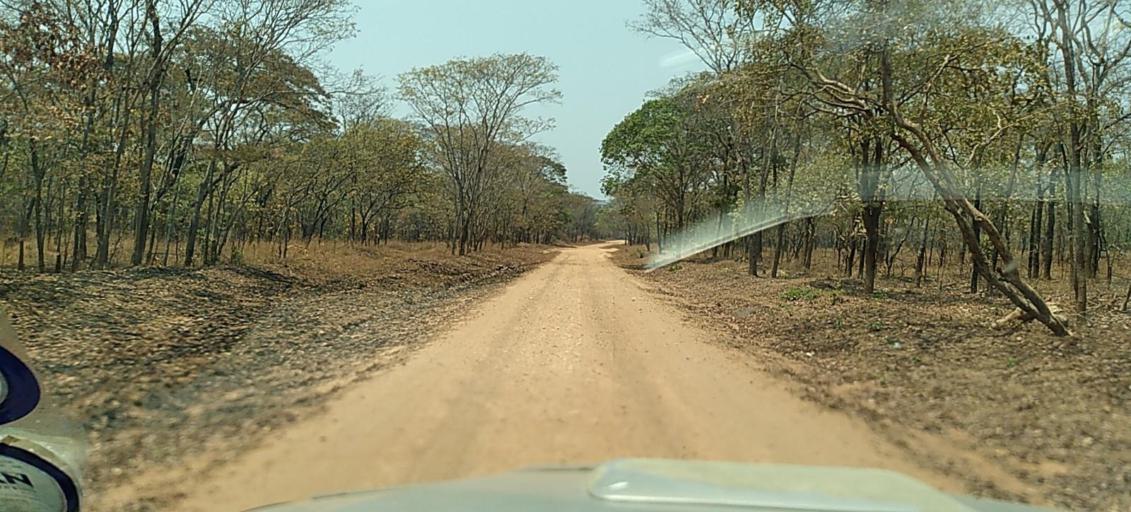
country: ZM
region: North-Western
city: Kasempa
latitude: -13.5567
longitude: 26.0737
